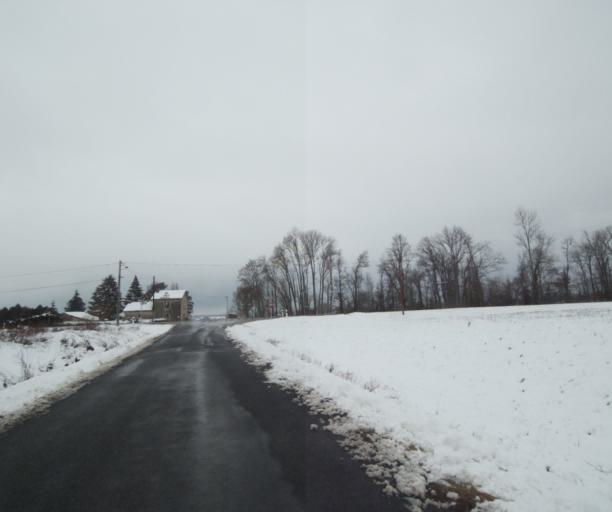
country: FR
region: Champagne-Ardenne
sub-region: Departement de la Haute-Marne
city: Laneuville-a-Remy
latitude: 48.4926
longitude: 4.8680
